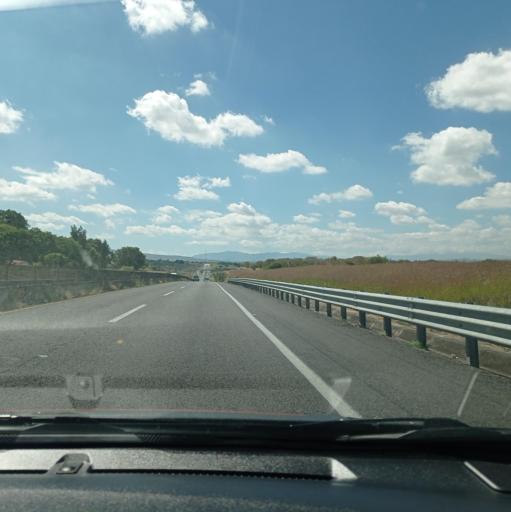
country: MX
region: Jalisco
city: Zapotlanejo
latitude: 20.6292
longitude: -103.0932
